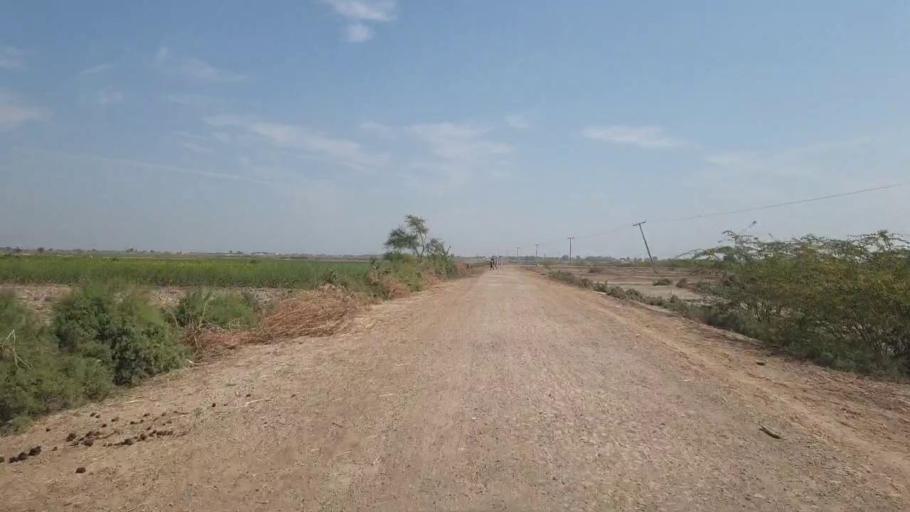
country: PK
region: Sindh
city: Mirwah Gorchani
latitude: 25.4359
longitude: 69.1939
